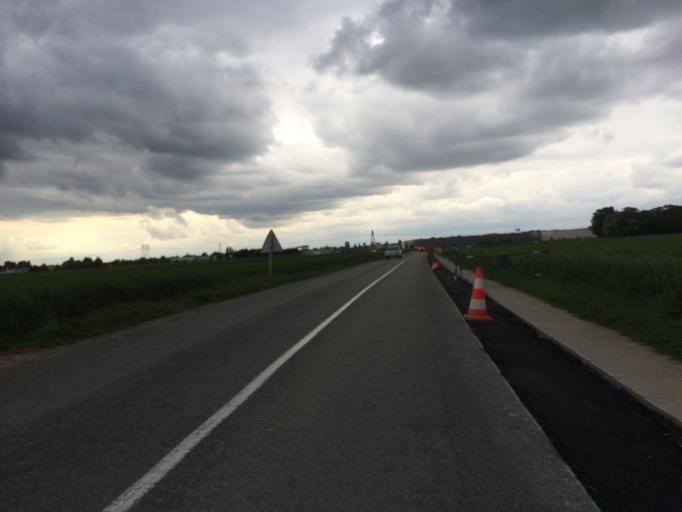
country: FR
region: Ile-de-France
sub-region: Departement de l'Essonne
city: Le Plessis-Pate
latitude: 48.6138
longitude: 2.3436
